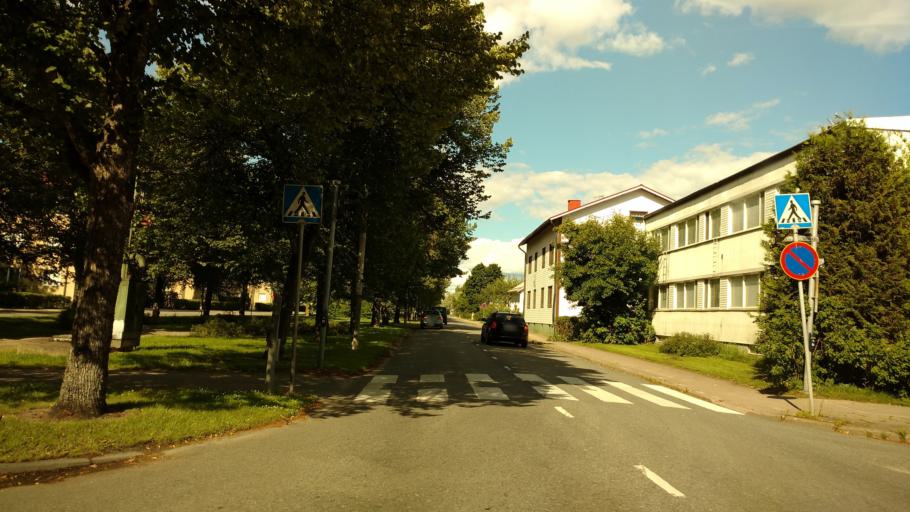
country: FI
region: Varsinais-Suomi
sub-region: Salo
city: Salo
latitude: 60.3881
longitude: 23.1402
